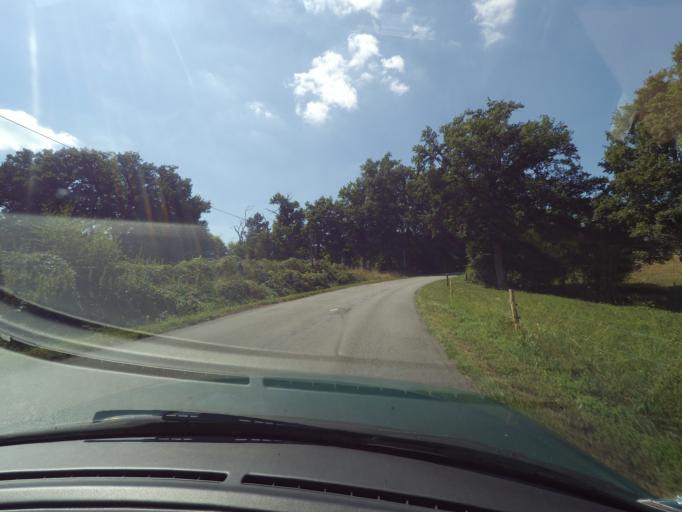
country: FR
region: Limousin
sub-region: Departement de la Haute-Vienne
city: Bosmie-l'Aiguille
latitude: 45.7755
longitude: 1.1825
